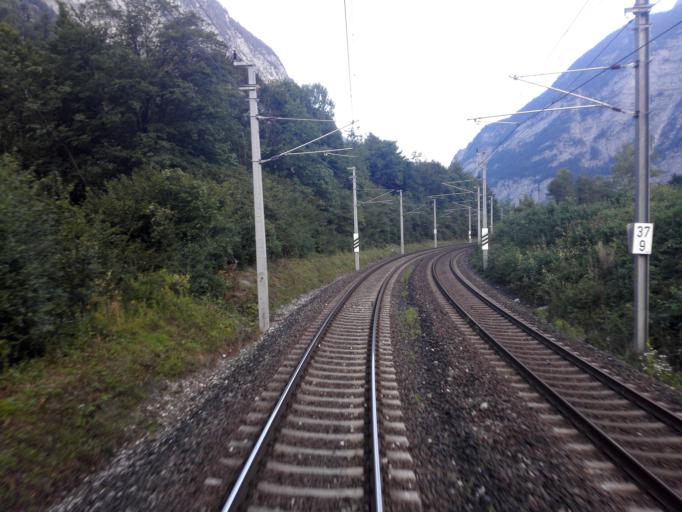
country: AT
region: Salzburg
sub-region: Politischer Bezirk Sankt Johann im Pongau
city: Werfen
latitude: 47.5310
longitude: 13.1657
